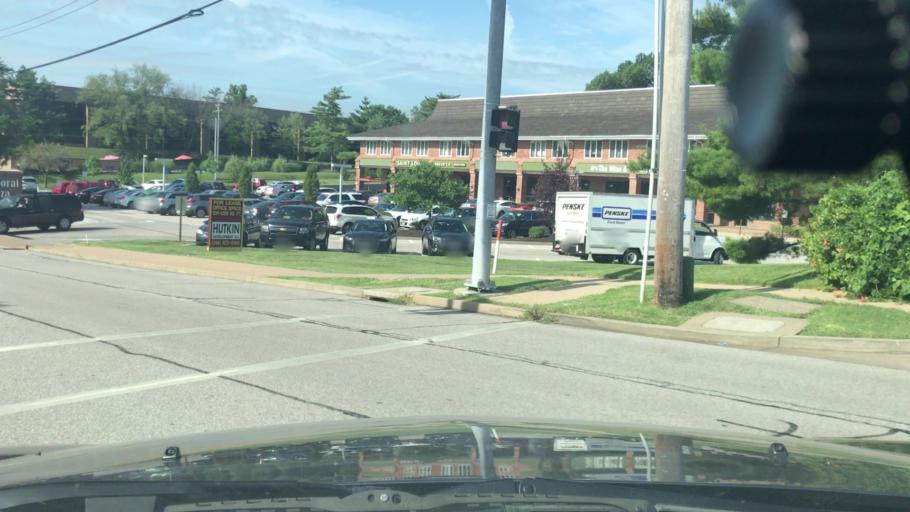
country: US
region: Missouri
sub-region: Saint Louis County
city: Creve Coeur
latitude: 38.6648
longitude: -90.4433
